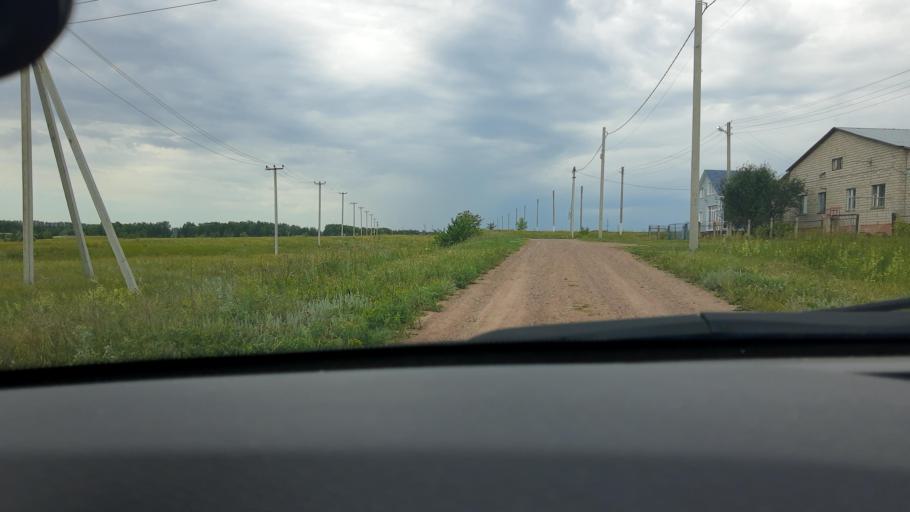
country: RU
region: Bashkortostan
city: Avdon
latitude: 54.5984
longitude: 55.7874
